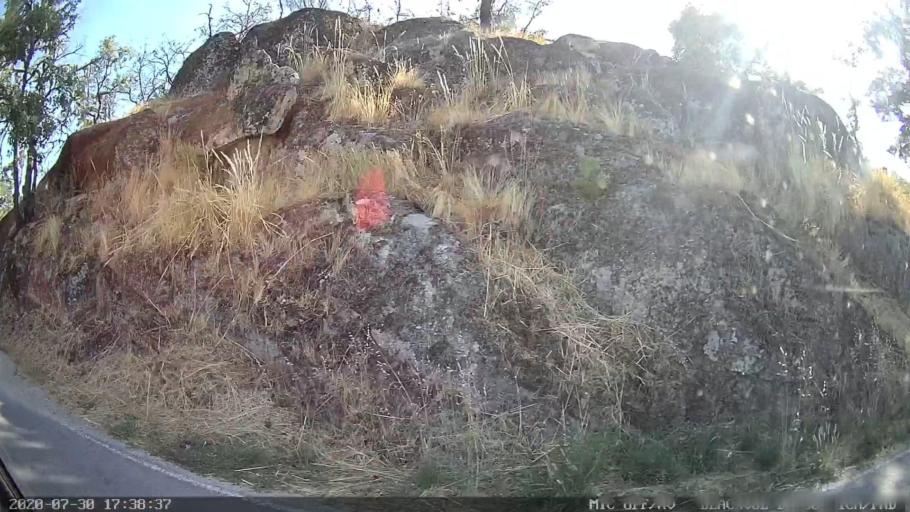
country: PT
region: Vila Real
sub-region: Murca
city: Murca
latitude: 41.3724
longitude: -7.5030
